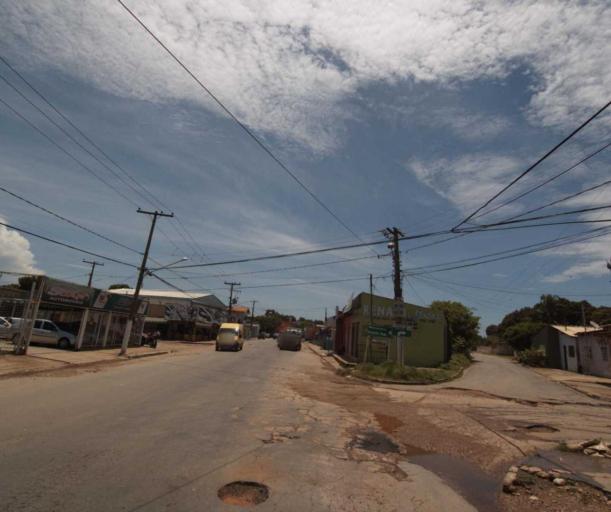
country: BR
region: Mato Grosso
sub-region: Varzea Grande
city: Varzea Grande
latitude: -15.6295
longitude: -56.1117
